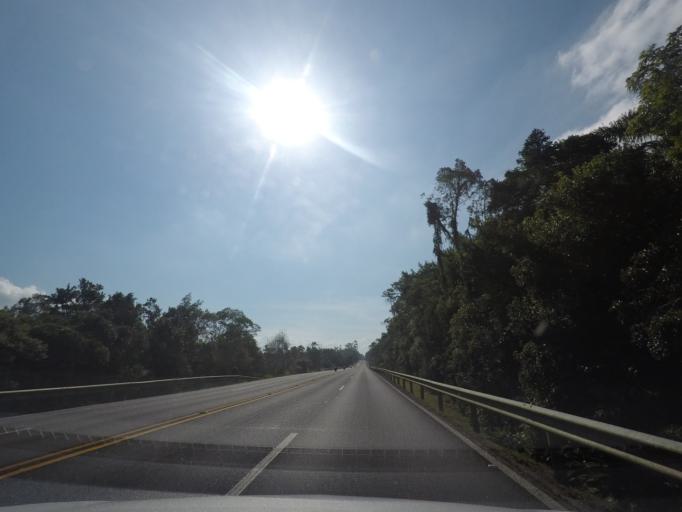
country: BR
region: Parana
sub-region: Pontal Do Parana
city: Pontal do Parana
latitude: -25.6140
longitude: -48.6033
